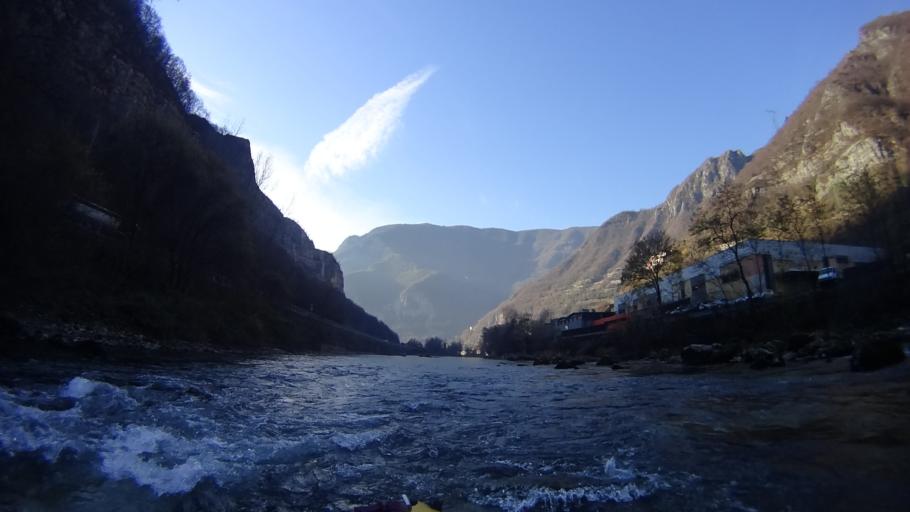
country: IT
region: Veneto
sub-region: Provincia di Vicenza
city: Valstagna
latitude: 45.8685
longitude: 11.6674
